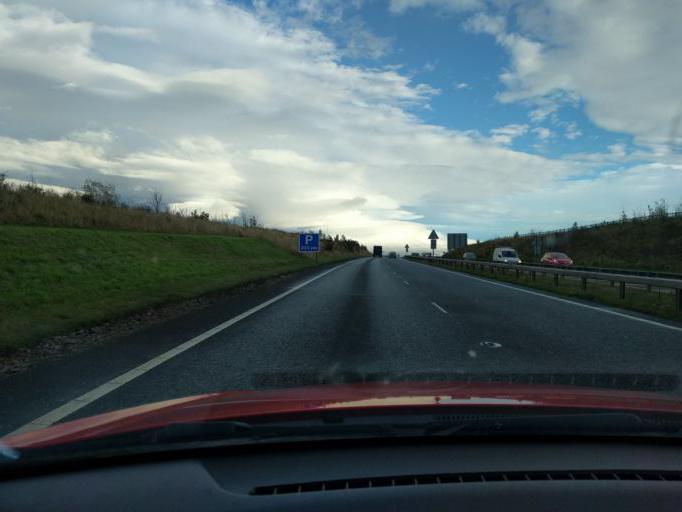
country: GB
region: Scotland
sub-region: East Lothian
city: Dunbar
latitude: 55.9891
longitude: -2.5594
